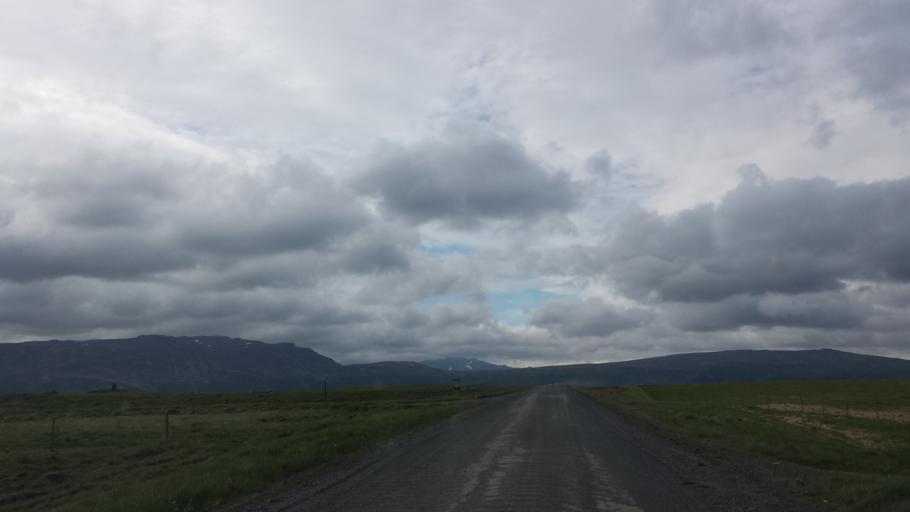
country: IS
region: South
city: Selfoss
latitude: 64.2883
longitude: -20.2288
